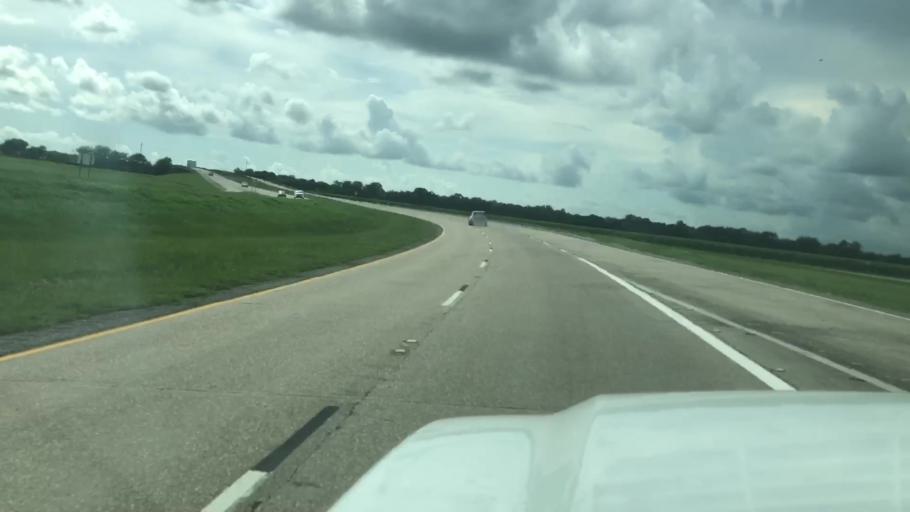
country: US
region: Louisiana
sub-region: Saint Mary Parish
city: Franklin
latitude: 29.7582
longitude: -91.4581
